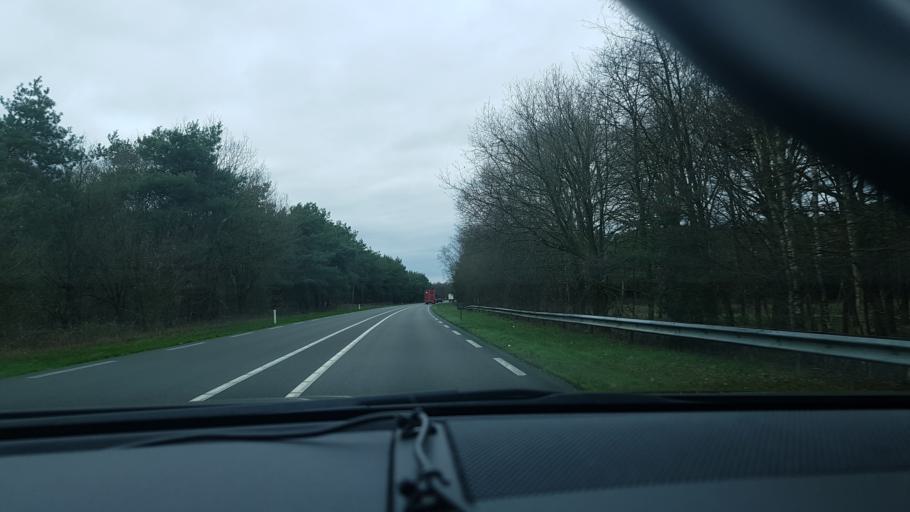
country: NL
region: North Brabant
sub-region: Gemeente Asten
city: Asten
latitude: 51.4312
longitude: 5.7423
